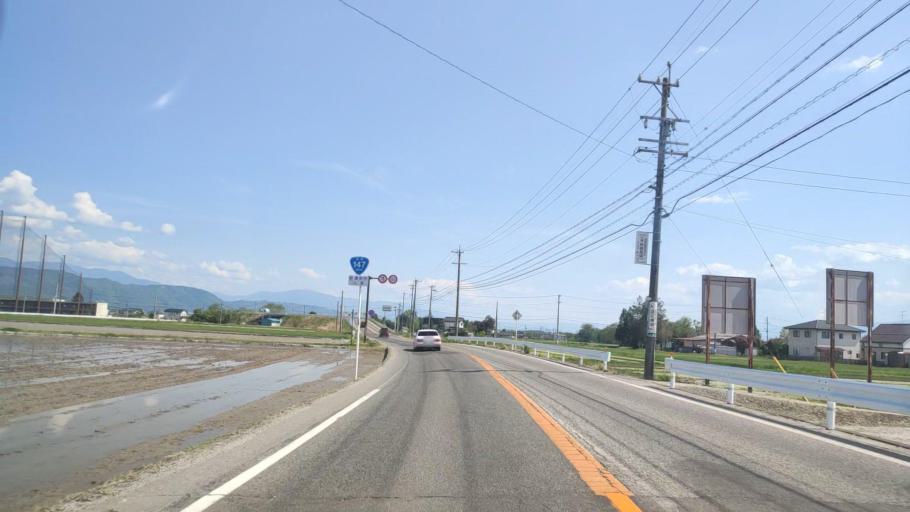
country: JP
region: Nagano
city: Hotaka
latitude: 36.3795
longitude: 137.8685
